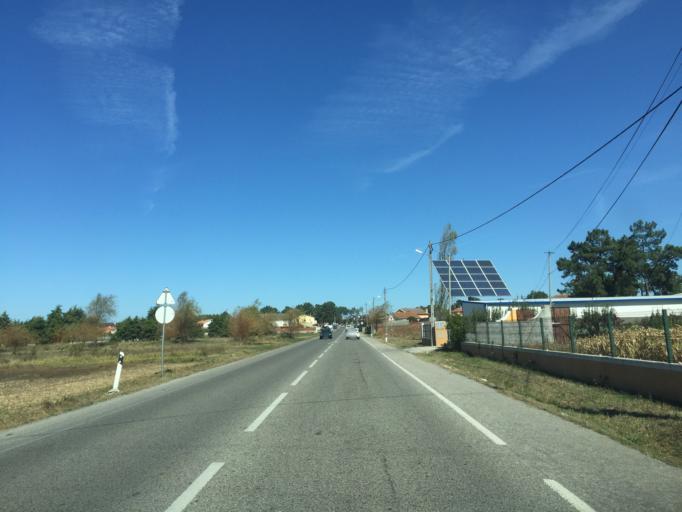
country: PT
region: Coimbra
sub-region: Figueira da Foz
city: Alhadas
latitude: 40.2536
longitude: -8.7825
